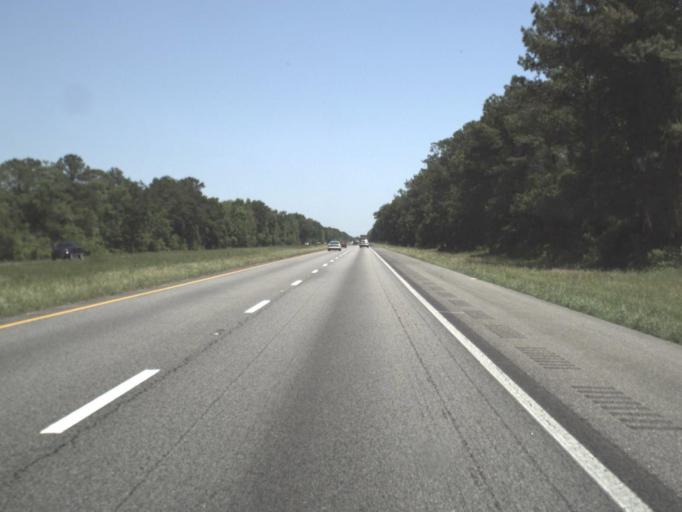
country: US
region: Florida
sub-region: Jefferson County
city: Monticello
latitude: 30.4695
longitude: -83.8122
